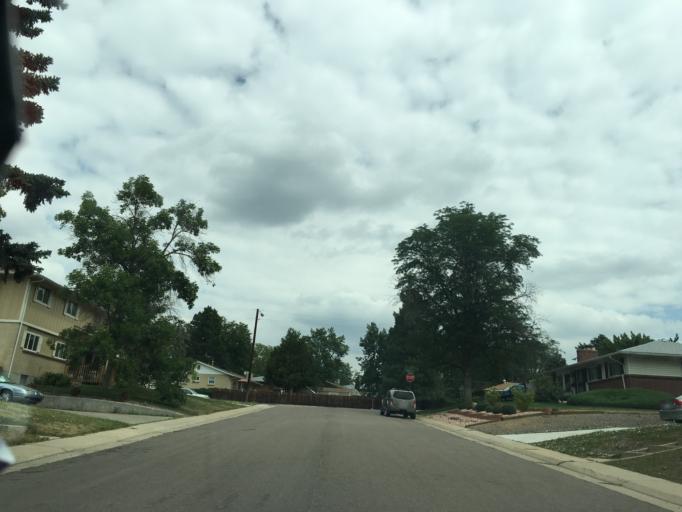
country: US
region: Colorado
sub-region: Arapahoe County
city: Sheridan
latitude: 39.6629
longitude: -105.0384
